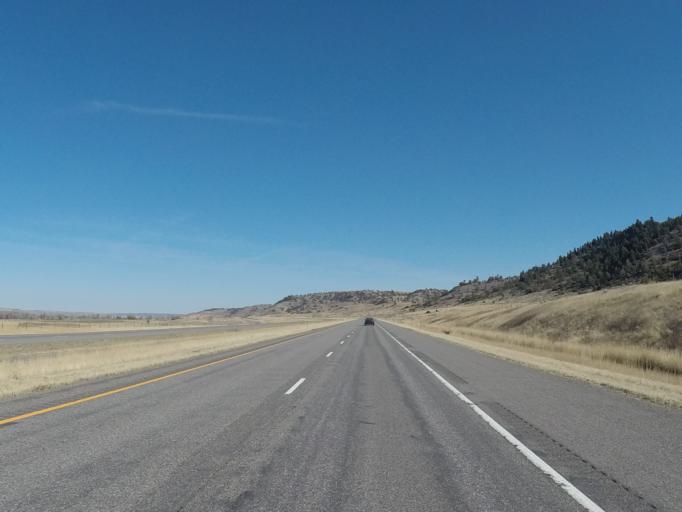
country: US
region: Montana
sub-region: Sweet Grass County
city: Big Timber
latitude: 45.7635
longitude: -110.0999
